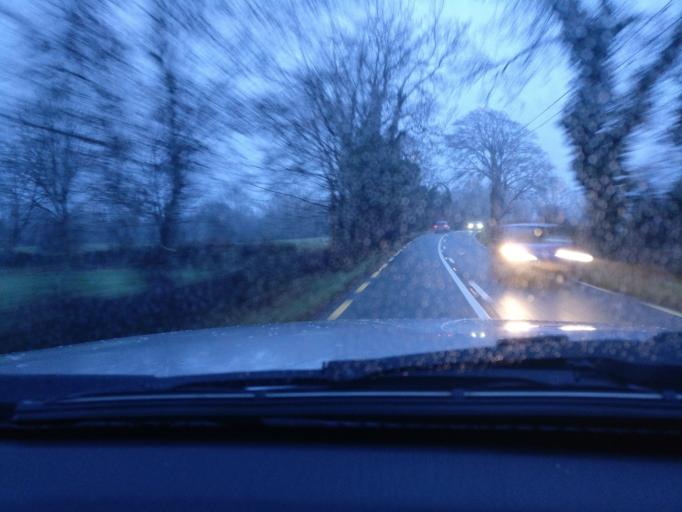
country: IE
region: Leinster
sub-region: An Mhi
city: Athboy
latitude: 53.6403
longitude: -6.8346
